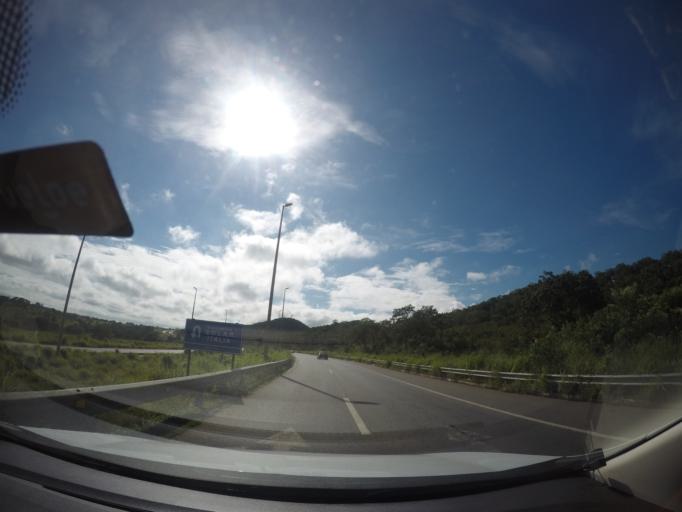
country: BR
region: Goias
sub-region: Senador Canedo
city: Senador Canedo
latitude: -16.6836
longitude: -49.1328
